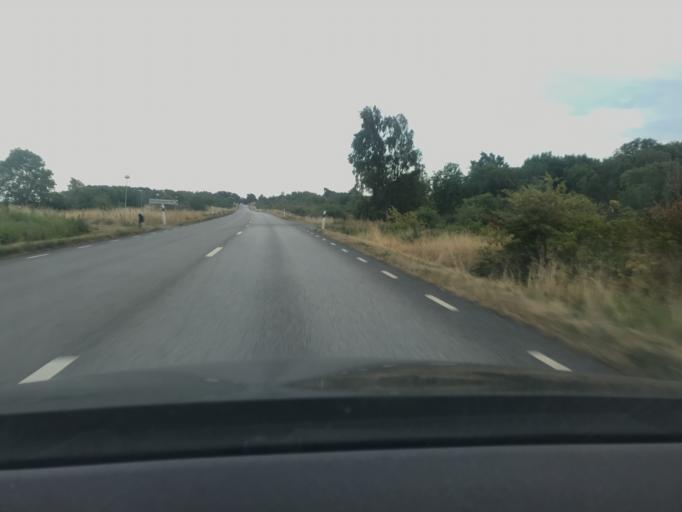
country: SE
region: Skane
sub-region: Simrishamns Kommun
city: Simrishamn
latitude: 55.5829
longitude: 14.3270
